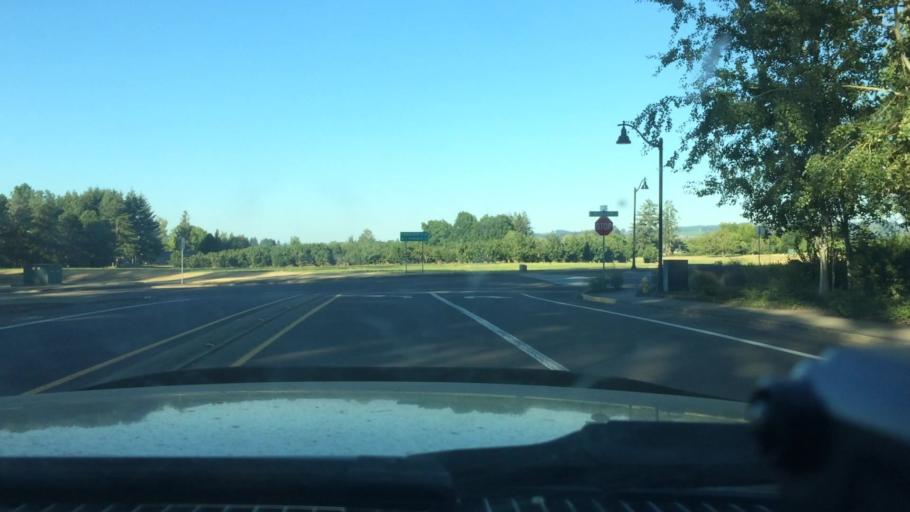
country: US
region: Oregon
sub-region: Yamhill County
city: Newberg
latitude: 45.3184
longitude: -122.9479
